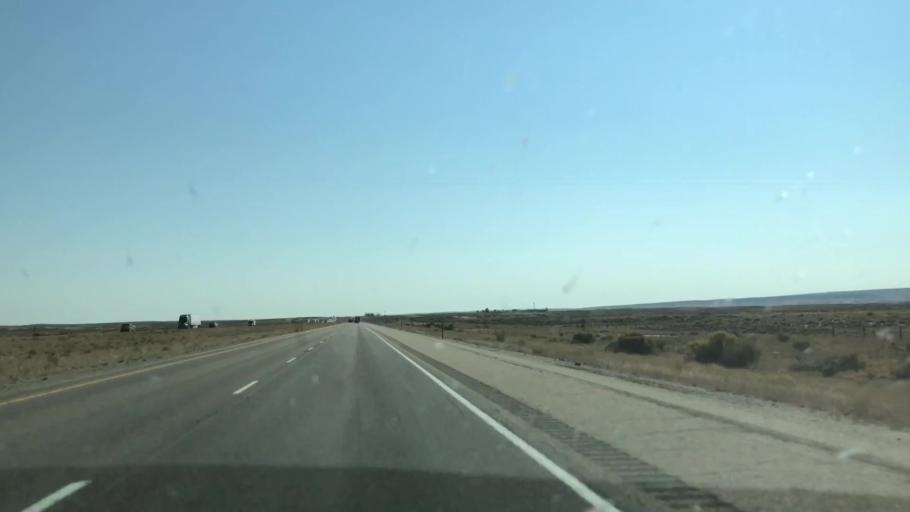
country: US
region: Wyoming
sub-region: Sweetwater County
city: Rock Springs
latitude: 41.6367
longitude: -108.4372
